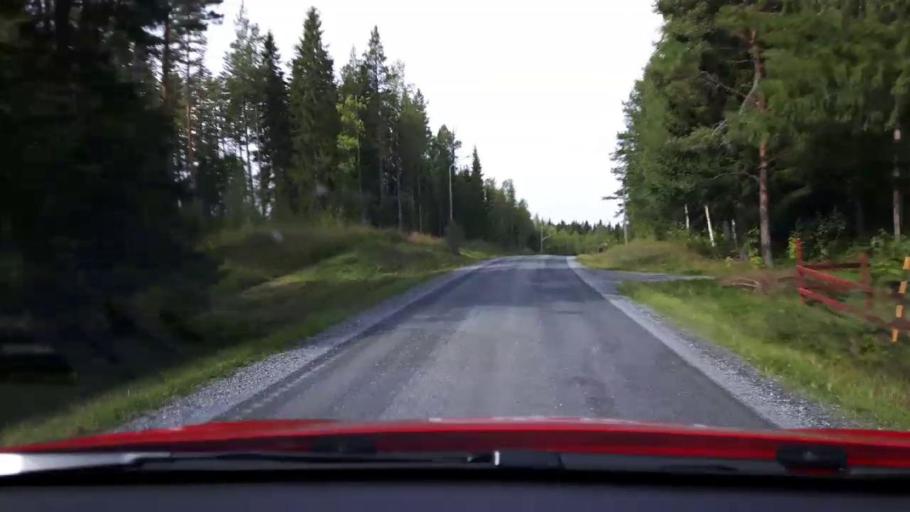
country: SE
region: Jaemtland
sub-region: Krokoms Kommun
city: Valla
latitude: 63.2593
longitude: 13.9278
